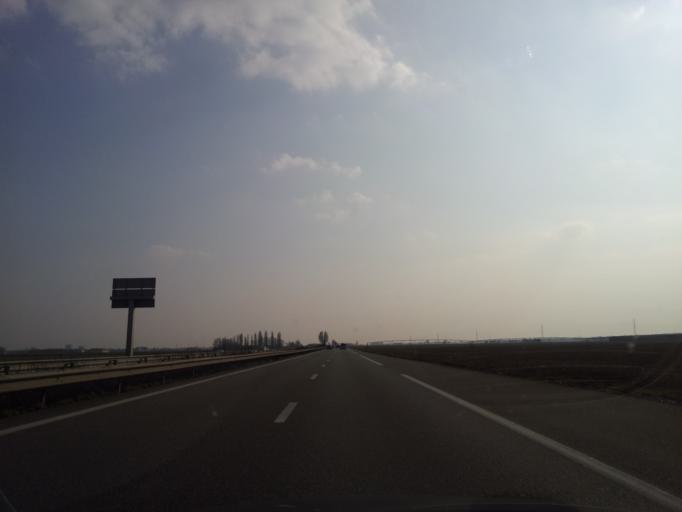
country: FR
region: Alsace
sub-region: Departement du Haut-Rhin
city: Sainte-Croix-en-Plaine
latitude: 47.9872
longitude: 7.3769
